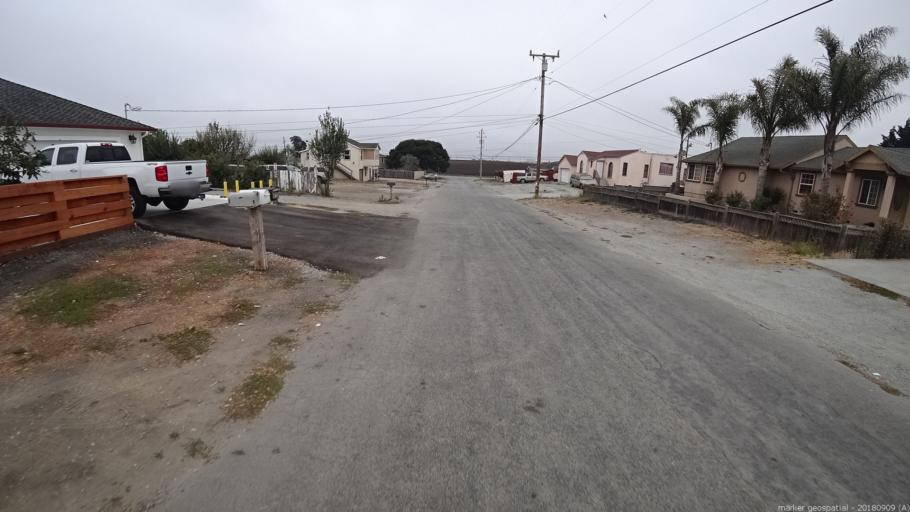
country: US
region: California
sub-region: Monterey County
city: Boronda
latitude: 36.7016
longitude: -121.6742
